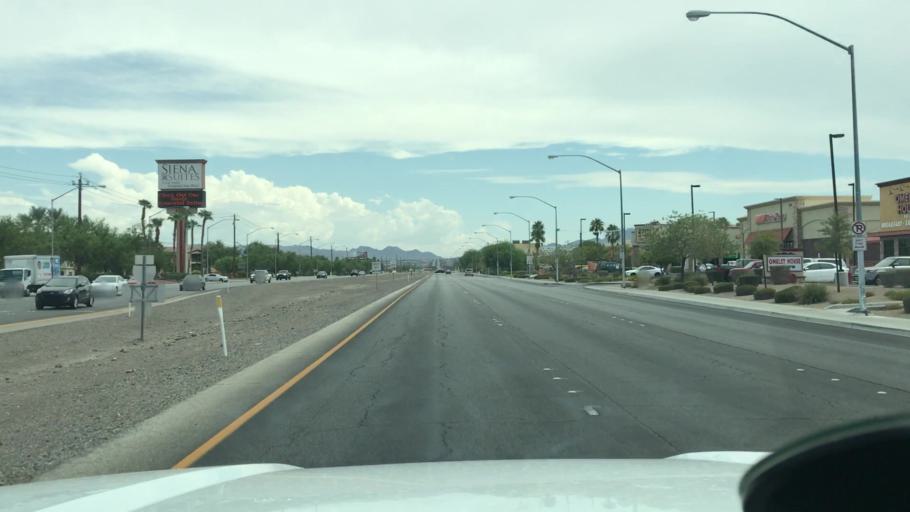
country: US
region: Nevada
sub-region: Clark County
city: Whitney
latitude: 36.0837
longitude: -115.0318
